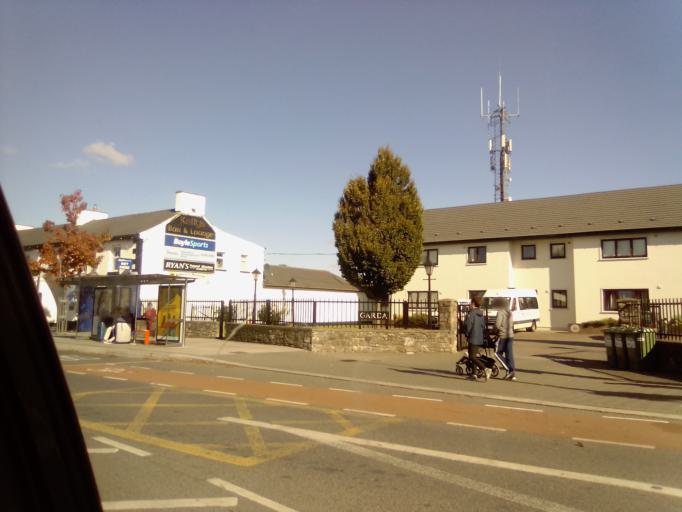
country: IE
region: Leinster
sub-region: An Mhi
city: Ashbourne
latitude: 53.5111
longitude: -6.3974
